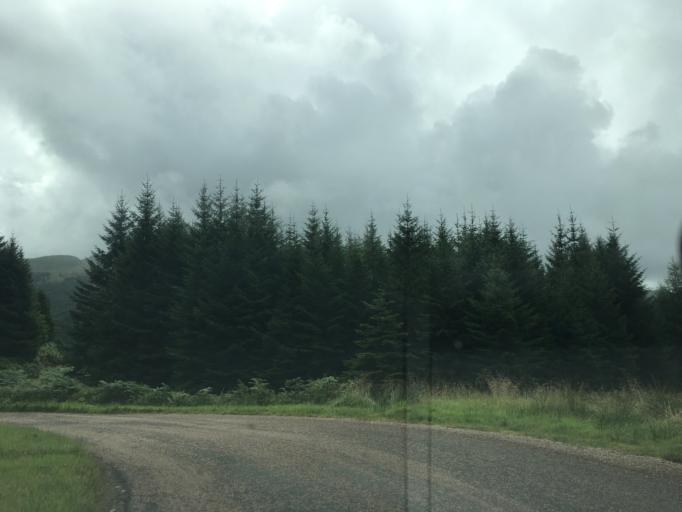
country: GB
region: Scotland
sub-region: Argyll and Bute
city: Oban
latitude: 56.2495
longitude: -5.4321
